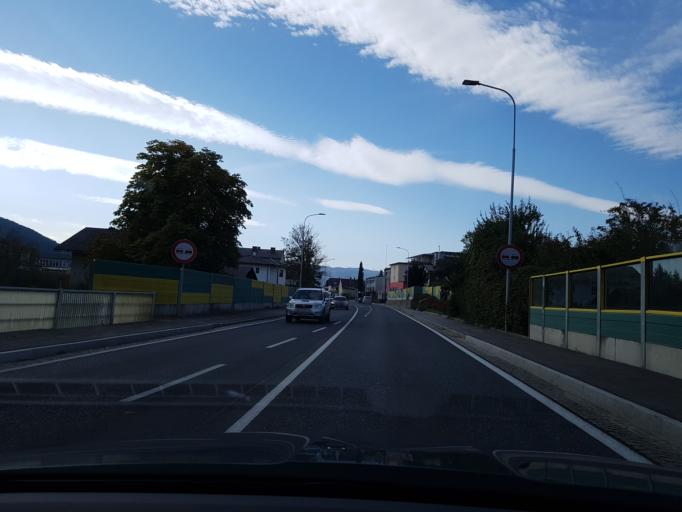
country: AT
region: Carinthia
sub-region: Politischer Bezirk Feldkirchen
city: Feldkirchen in Karnten
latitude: 46.7298
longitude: 14.0923
